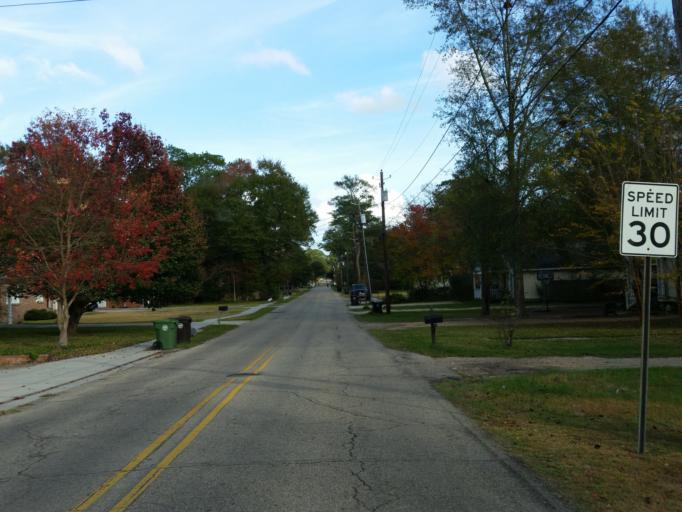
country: US
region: Mississippi
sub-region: Forrest County
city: Hattiesburg
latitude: 31.3195
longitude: -89.3225
